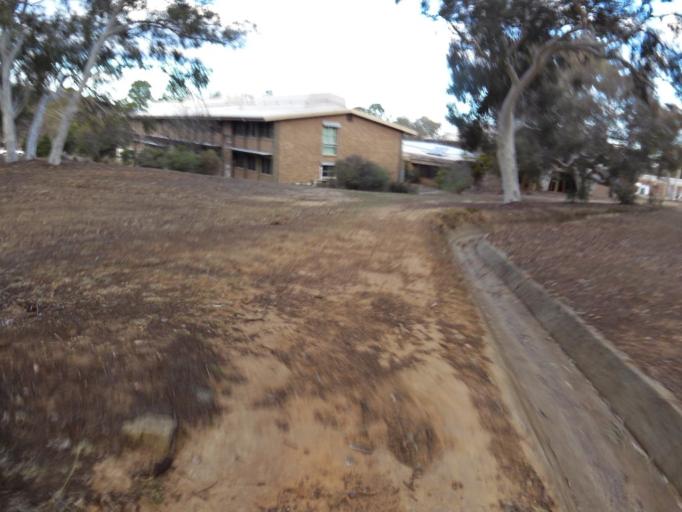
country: AU
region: Australian Capital Territory
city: Acton
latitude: -35.2710
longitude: 149.1103
